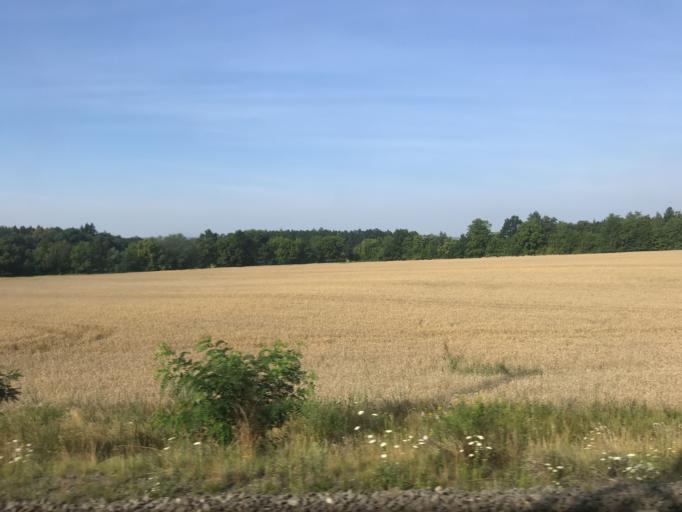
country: CZ
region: Jihocesky
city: Chotoviny
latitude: 49.4605
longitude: 14.6799
